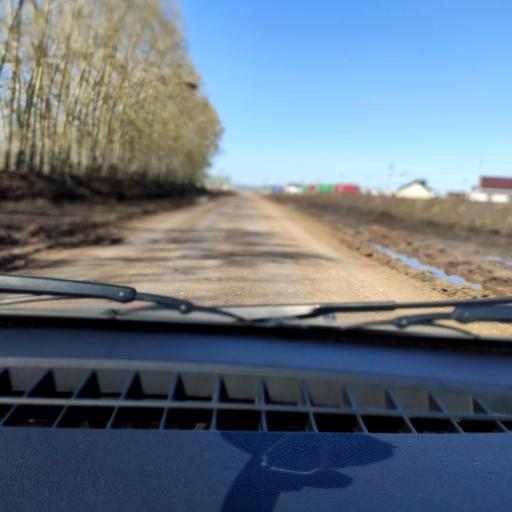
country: RU
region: Bashkortostan
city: Iglino
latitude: 54.8162
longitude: 56.4317
